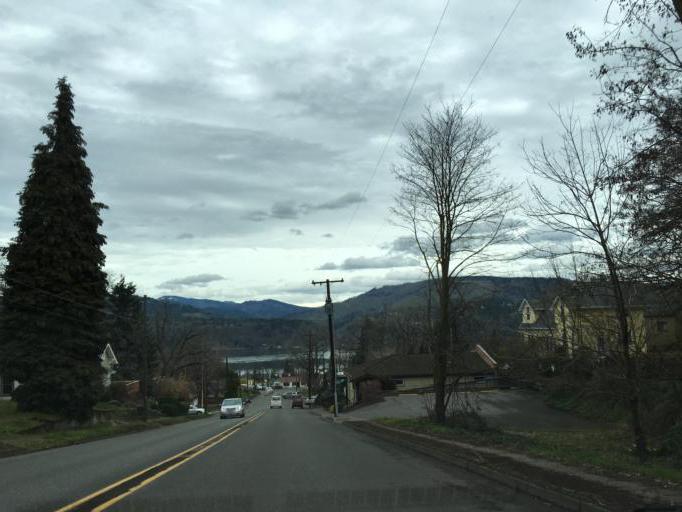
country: US
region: Oregon
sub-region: Hood River County
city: Hood River
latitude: 45.7066
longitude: -121.5251
